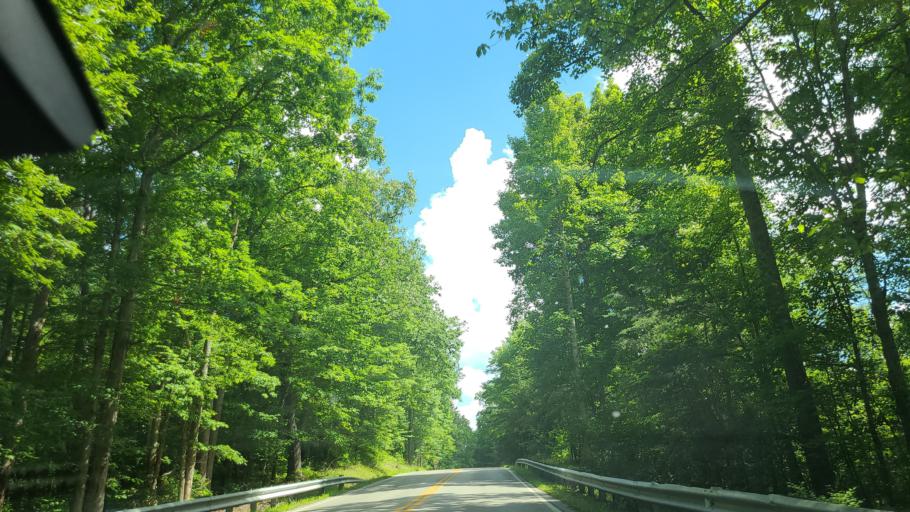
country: US
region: Kentucky
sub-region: Whitley County
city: Williamsburg
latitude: 36.8502
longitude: -84.2407
